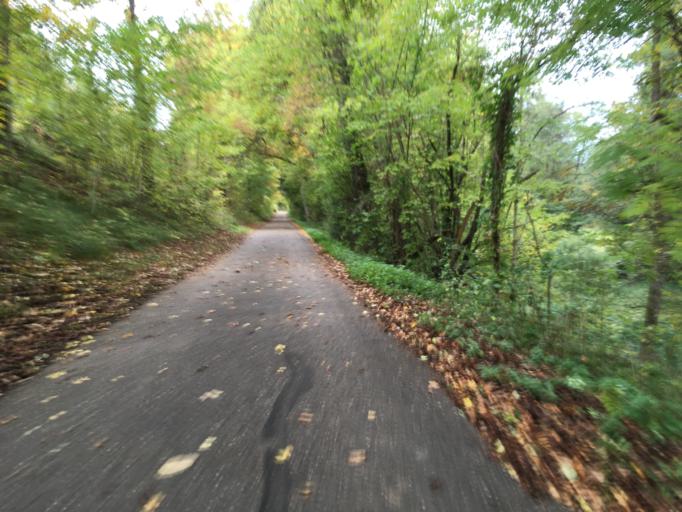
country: DE
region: Baden-Wuerttemberg
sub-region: Karlsruhe Region
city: Seckach
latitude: 49.4332
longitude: 9.3643
